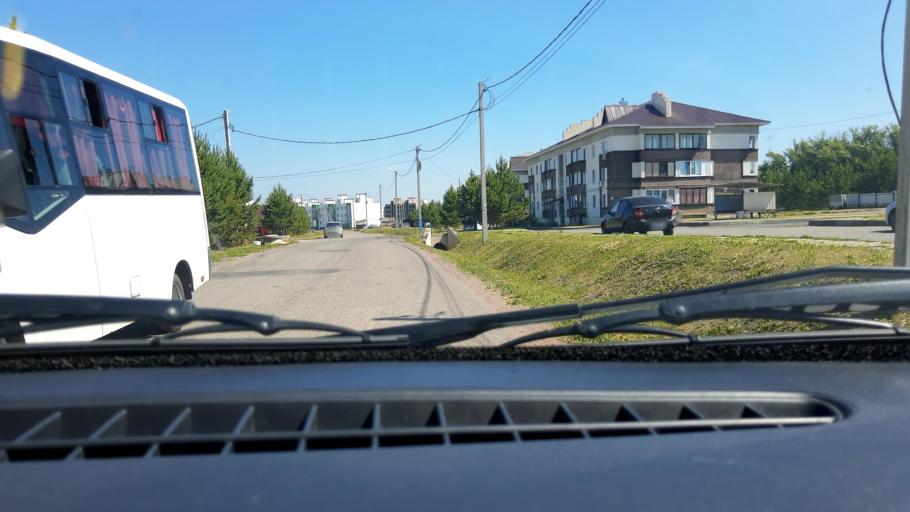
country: RU
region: Bashkortostan
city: Avdon
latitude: 54.4796
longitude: 55.8821
